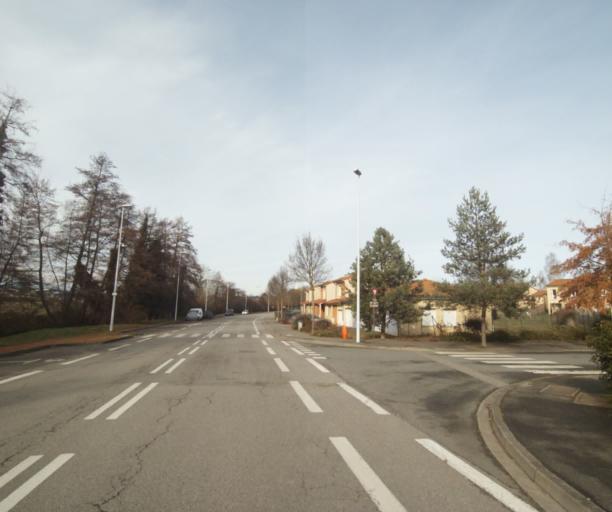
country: FR
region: Rhone-Alpes
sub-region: Departement de la Loire
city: Riorges
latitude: 46.0260
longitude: 4.0491
